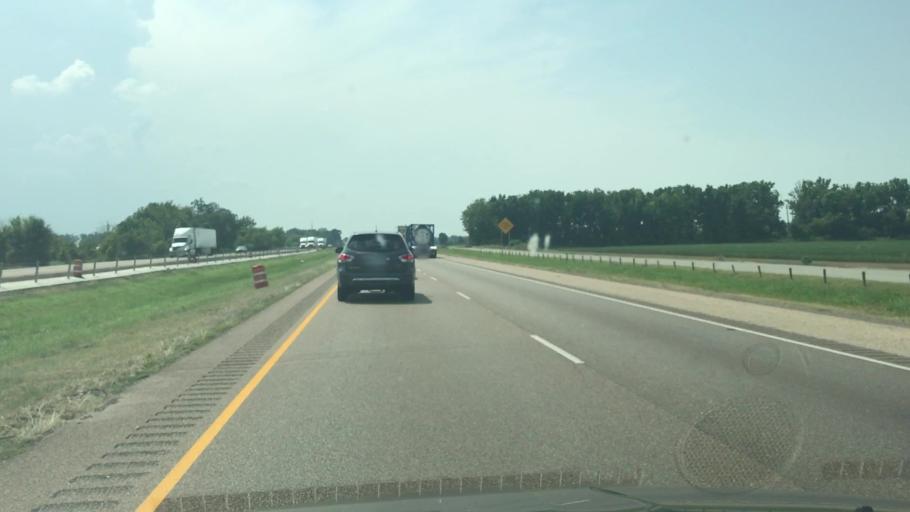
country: US
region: Arkansas
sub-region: Crittenden County
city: West Memphis
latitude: 35.1485
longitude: -90.3340
